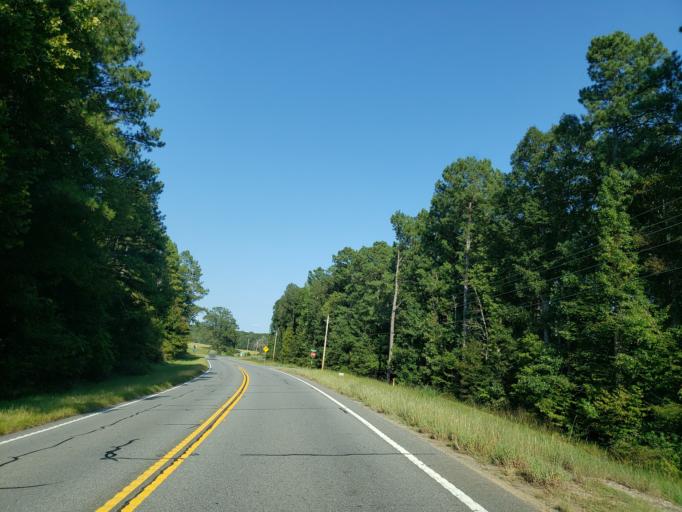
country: US
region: Georgia
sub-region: Whitfield County
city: Varnell
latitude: 34.8954
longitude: -84.9294
